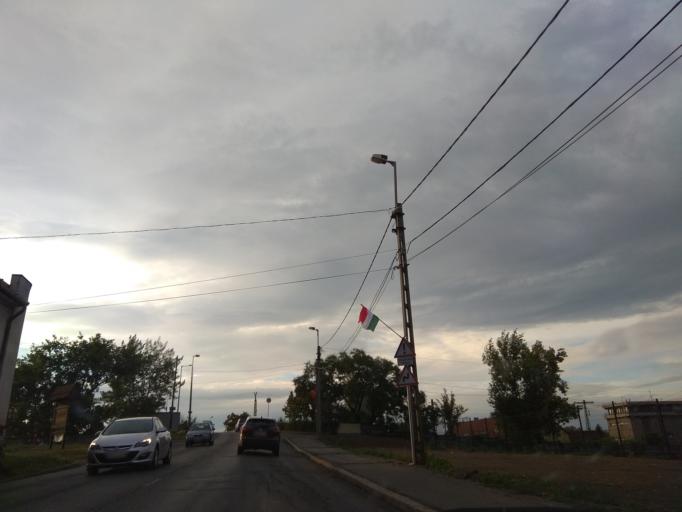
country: HU
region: Borsod-Abauj-Zemplen
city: Miskolc
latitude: 48.0962
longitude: 20.8036
